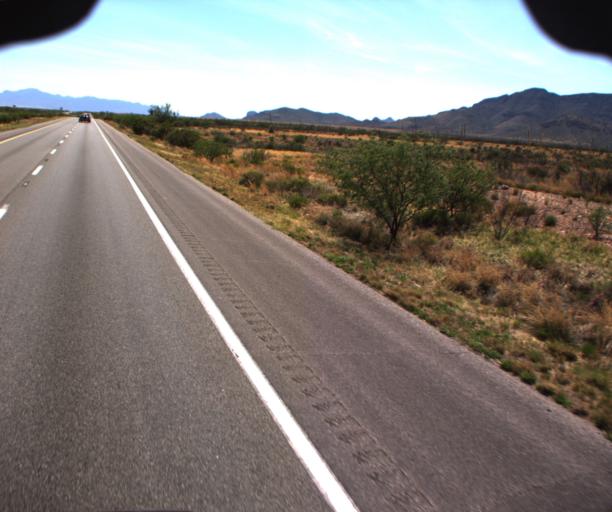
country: US
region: Arizona
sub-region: Cochise County
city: Whetstone
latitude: 31.8226
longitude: -110.3464
